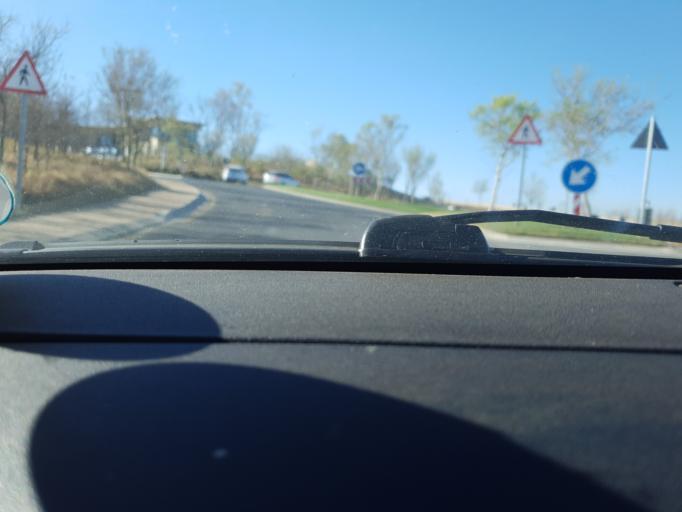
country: ZA
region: Gauteng
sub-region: City of Johannesburg Metropolitan Municipality
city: Diepsloot
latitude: -25.9791
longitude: 28.0126
